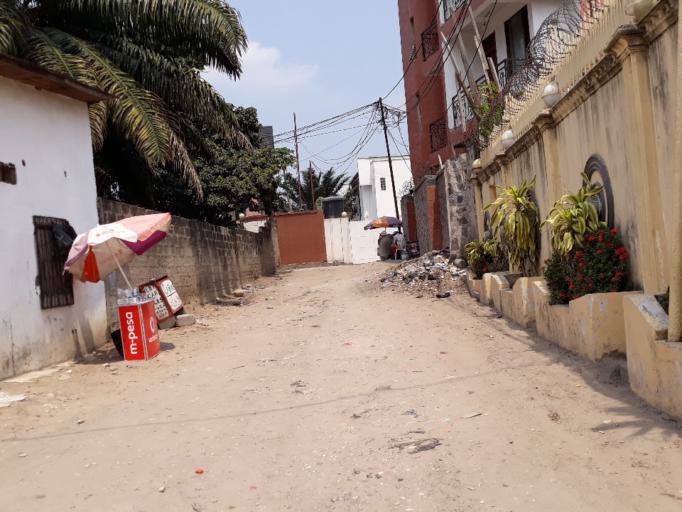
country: CD
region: Kinshasa
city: Kinshasa
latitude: -4.3275
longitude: 15.2779
